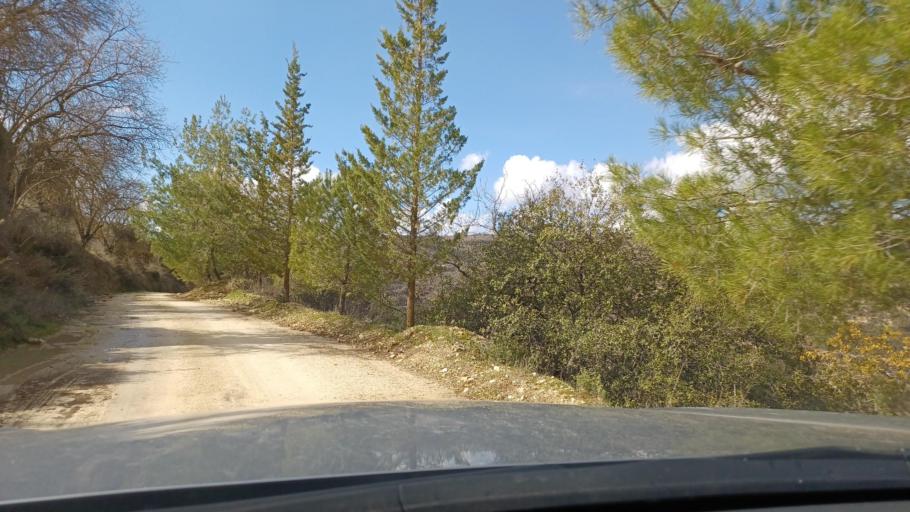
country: CY
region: Limassol
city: Pachna
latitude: 34.8384
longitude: 32.7682
